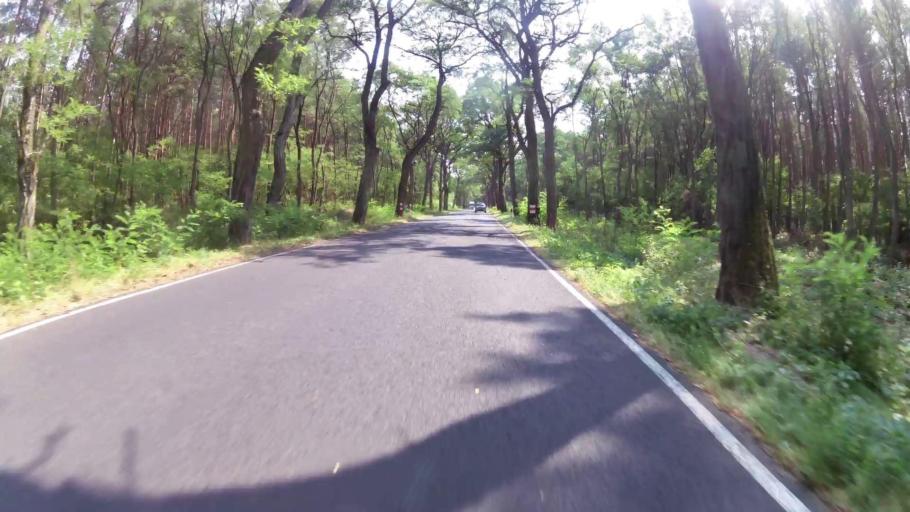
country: PL
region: West Pomeranian Voivodeship
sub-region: Powiat gryfinski
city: Moryn
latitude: 52.8332
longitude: 14.4143
